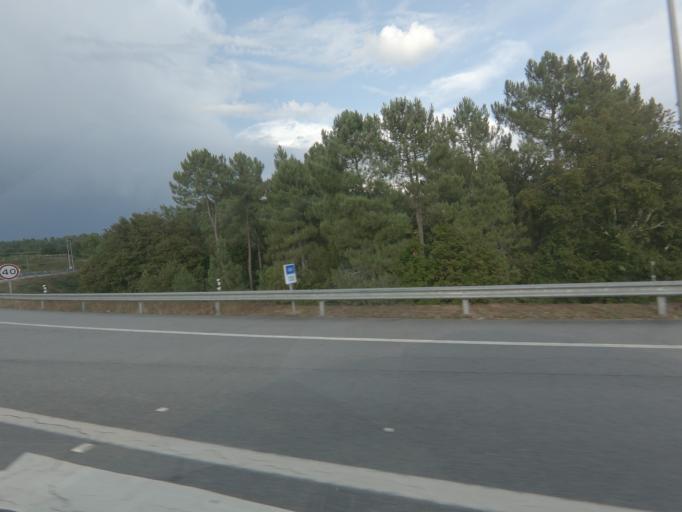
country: PT
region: Viseu
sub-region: Castro Daire
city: Castro Daire
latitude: 40.8564
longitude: -7.9290
